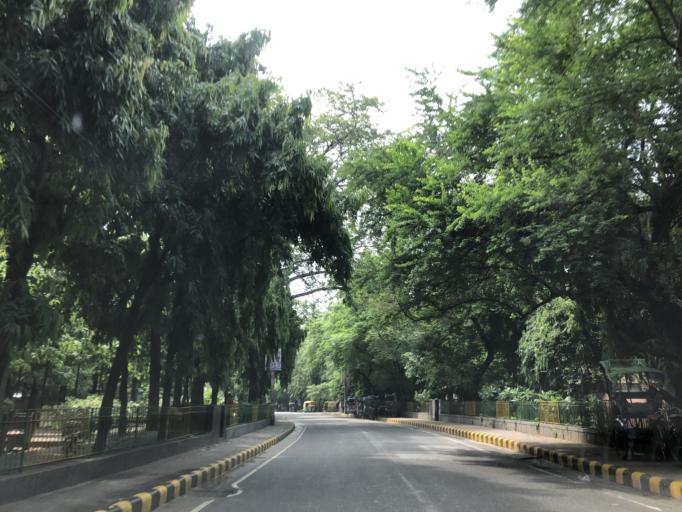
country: IN
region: NCT
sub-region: New Delhi
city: New Delhi
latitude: 28.5723
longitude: 77.2461
